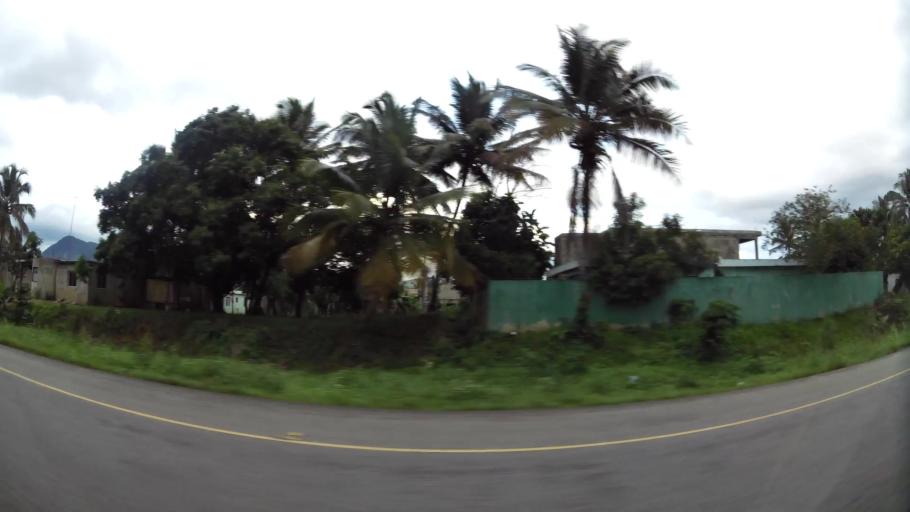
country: DO
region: San Cristobal
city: Villa Altagracia
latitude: 18.6414
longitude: -70.1686
